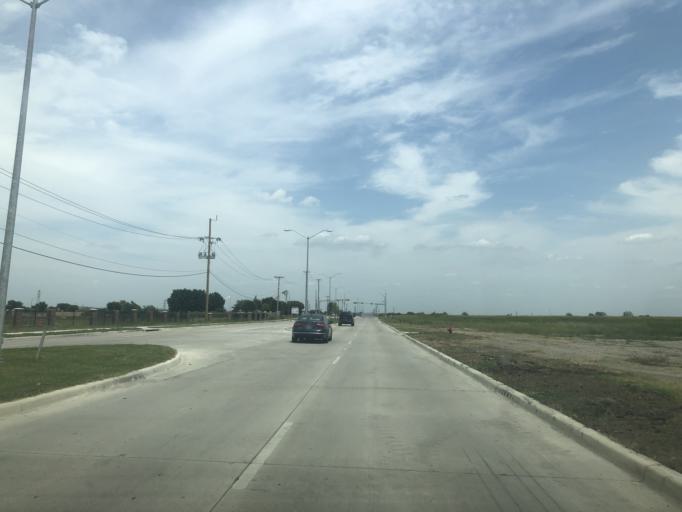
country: US
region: Texas
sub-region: Tarrant County
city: Saginaw
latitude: 32.8837
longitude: -97.3689
